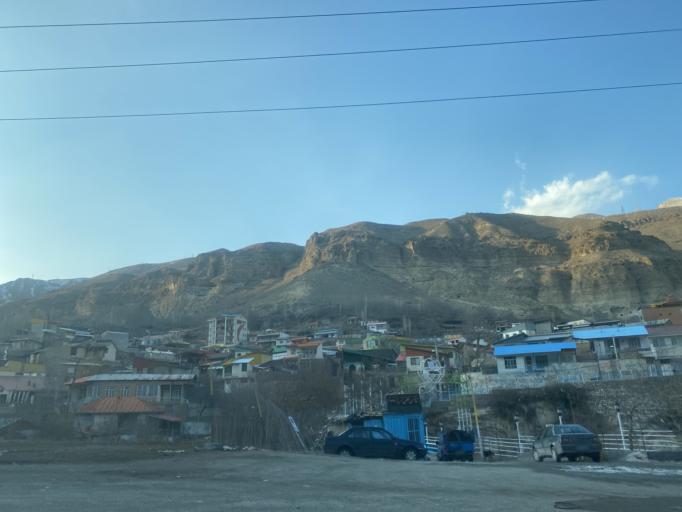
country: IR
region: Tehran
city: Damavand
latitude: 35.8686
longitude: 52.1560
